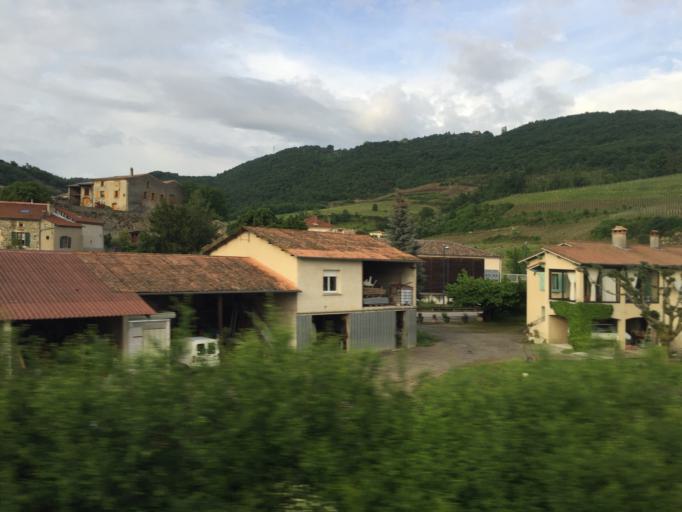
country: FR
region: Rhone-Alpes
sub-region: Departement de l'Ardeche
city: Saint-Jean-de-Muzols
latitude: 45.1061
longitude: 4.8317
